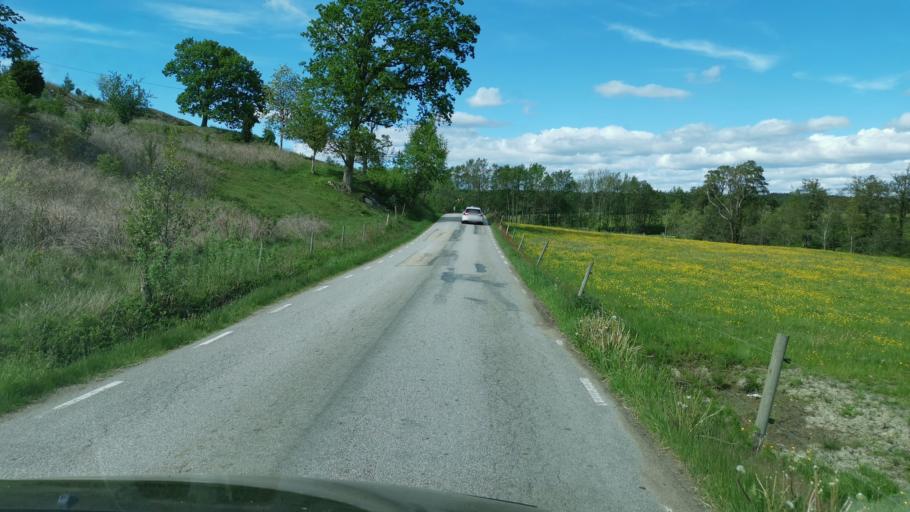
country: SE
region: Vaestra Goetaland
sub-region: Orust
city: Henan
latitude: 58.2740
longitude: 11.5992
